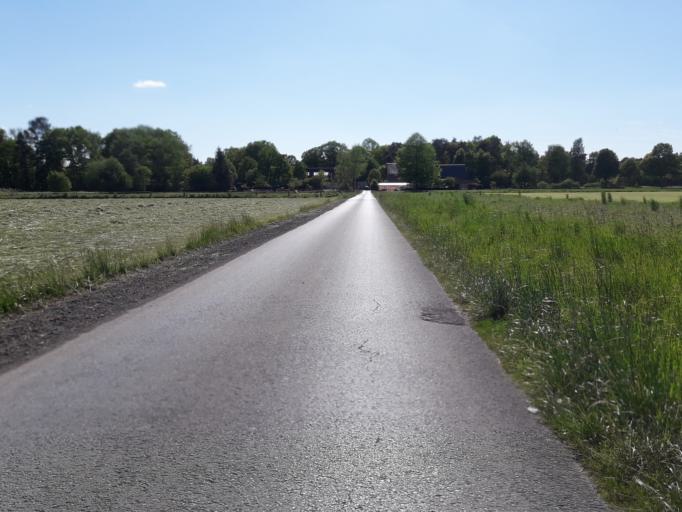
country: DE
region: North Rhine-Westphalia
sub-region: Regierungsbezirk Detmold
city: Delbruck
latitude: 51.7509
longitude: 8.5844
